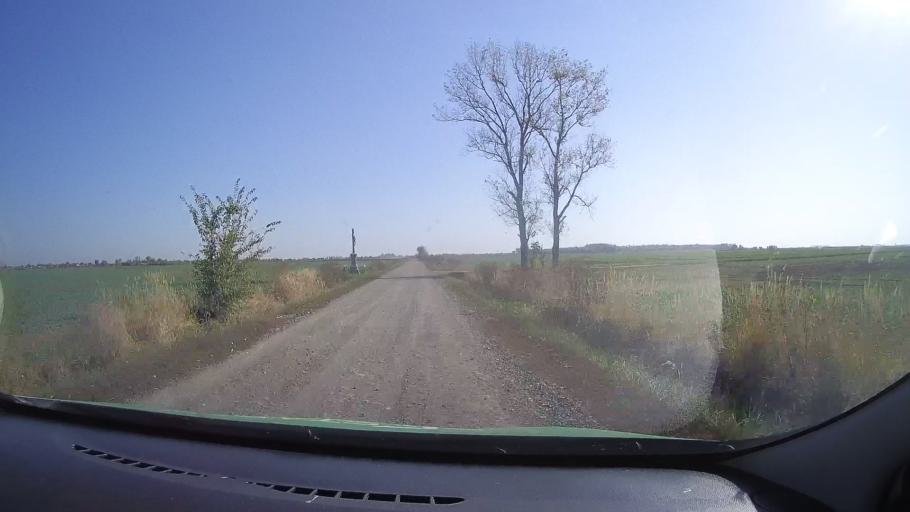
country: RO
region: Satu Mare
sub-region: Comuna Berveni
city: Berveni
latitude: 47.7354
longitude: 22.4503
